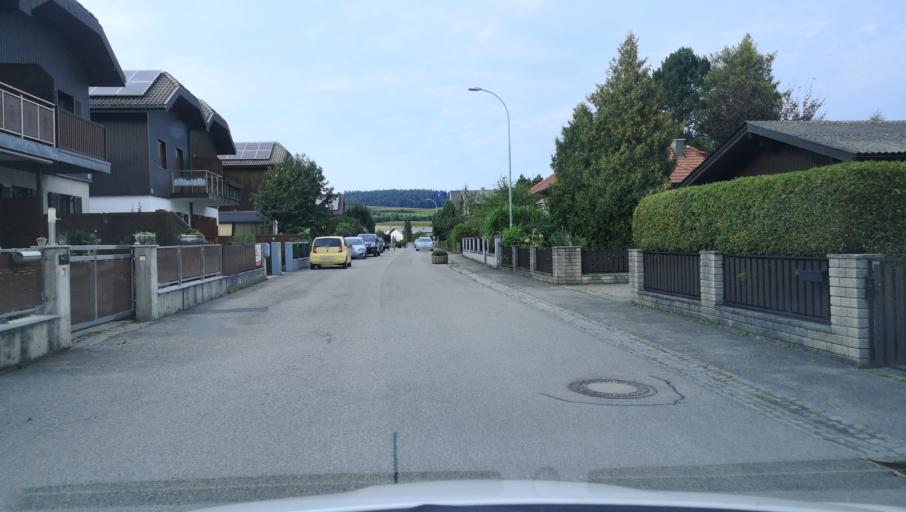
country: AT
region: Lower Austria
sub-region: Politischer Bezirk Melk
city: Blindenmarkt
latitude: 48.1298
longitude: 14.9843
